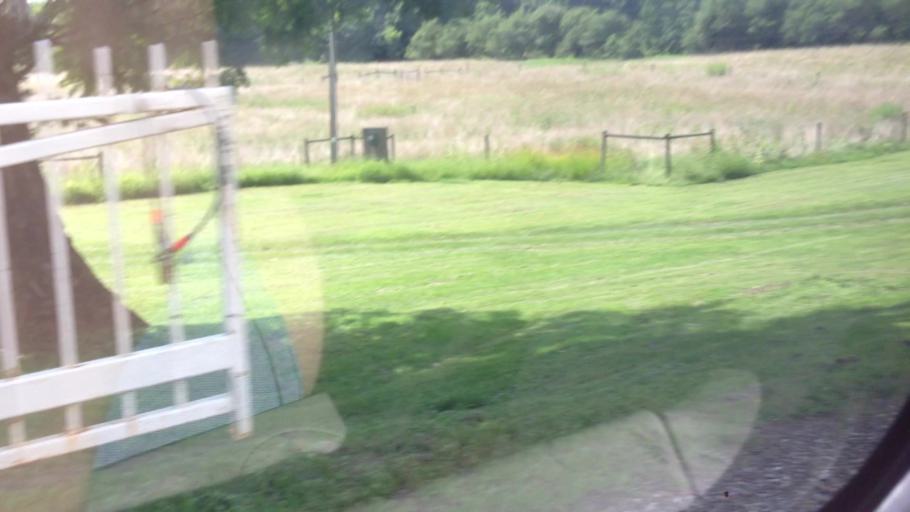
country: US
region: New York
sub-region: Dutchess County
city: Red Hook
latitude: 42.0096
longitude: -73.9106
